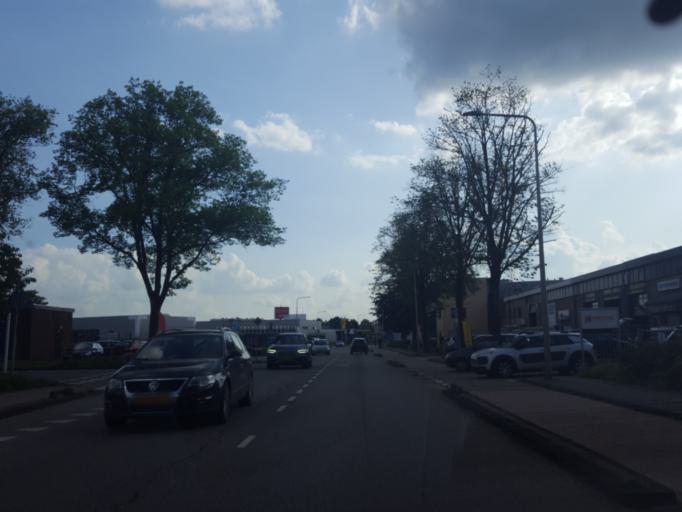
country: NL
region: Utrecht
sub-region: Gemeente Vianen
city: Vianen
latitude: 51.9835
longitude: 5.0995
